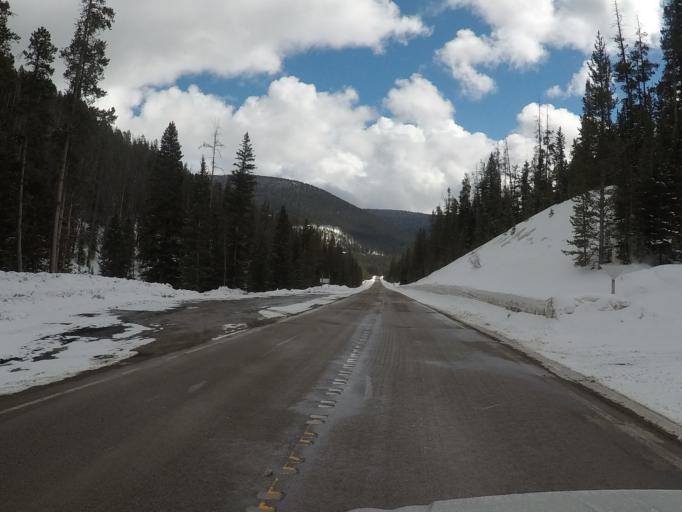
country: US
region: Montana
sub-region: Meagher County
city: White Sulphur Springs
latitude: 46.7991
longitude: -110.7035
